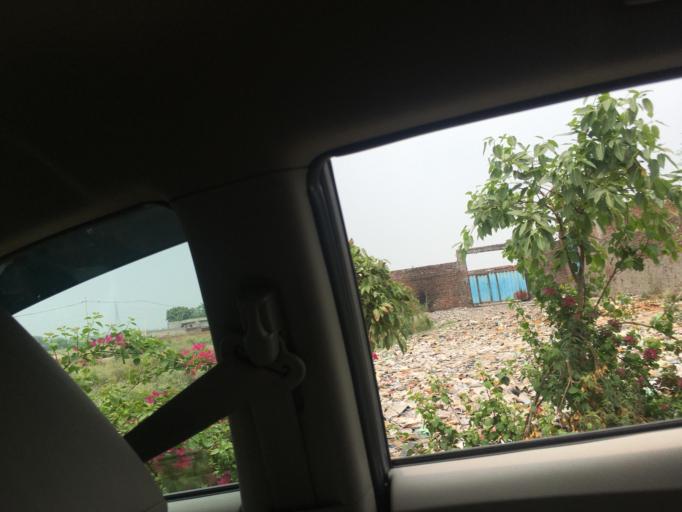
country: PK
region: Punjab
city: Lahore
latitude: 31.6174
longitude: 74.3549
